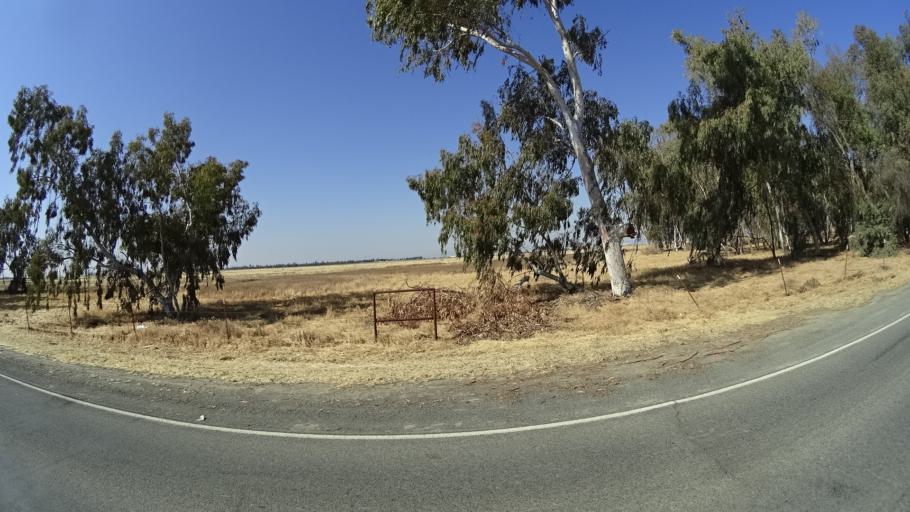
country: US
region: California
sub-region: Fresno County
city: Riverdale
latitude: 36.3610
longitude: -119.9122
